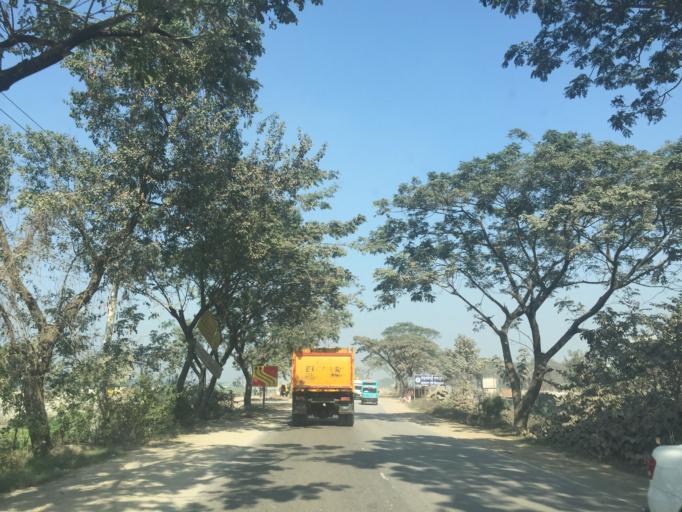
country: BD
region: Dhaka
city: Tungi
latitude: 23.8362
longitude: 90.3400
